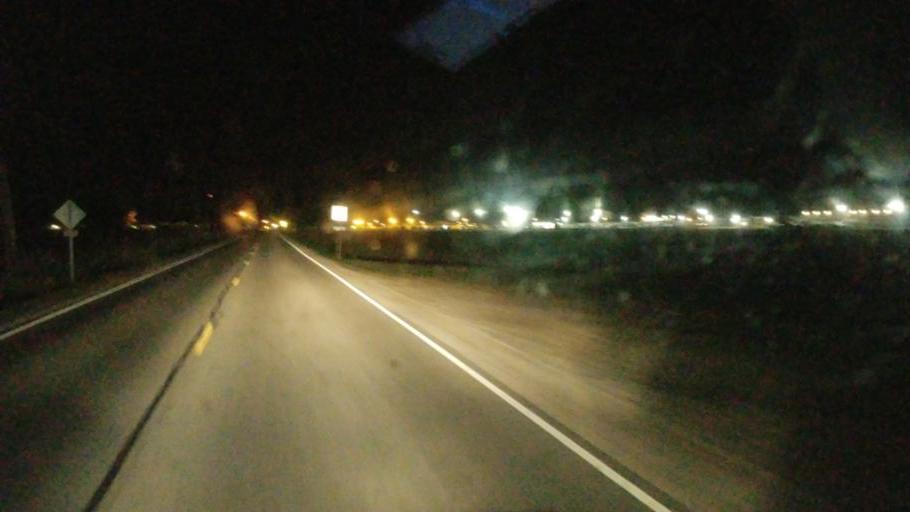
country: US
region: Ohio
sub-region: Marion County
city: Marion
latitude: 40.6152
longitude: -83.1032
